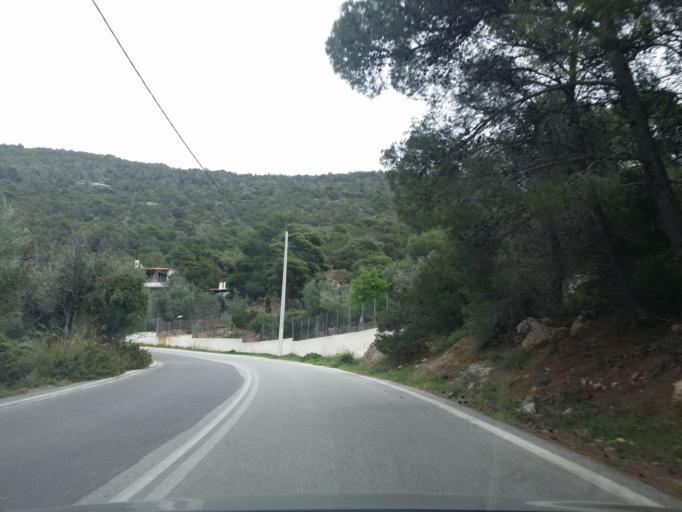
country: GR
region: Central Greece
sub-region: Nomos Voiotias
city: Kaparellion
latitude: 38.1474
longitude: 23.2350
